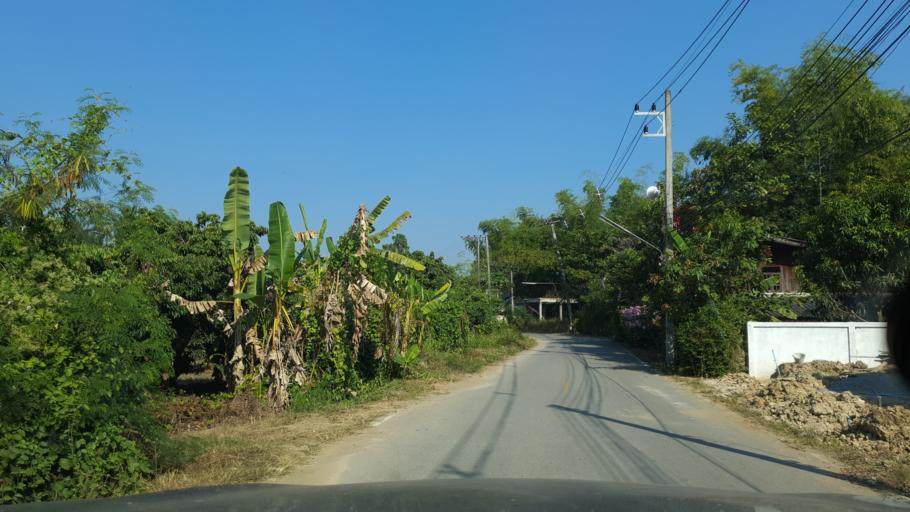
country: TH
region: Chiang Mai
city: Saraphi
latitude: 18.6986
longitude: 99.0778
